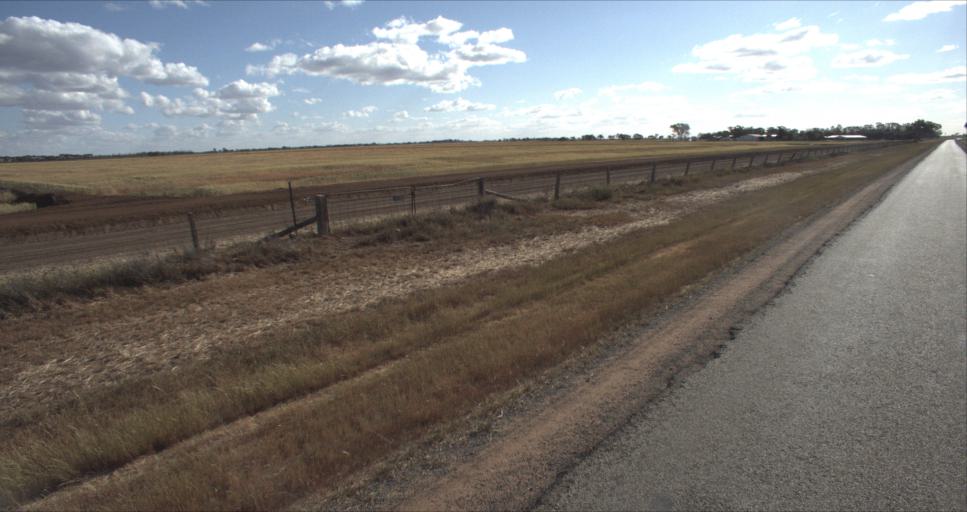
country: AU
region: New South Wales
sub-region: Leeton
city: Leeton
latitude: -34.4574
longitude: 146.2932
